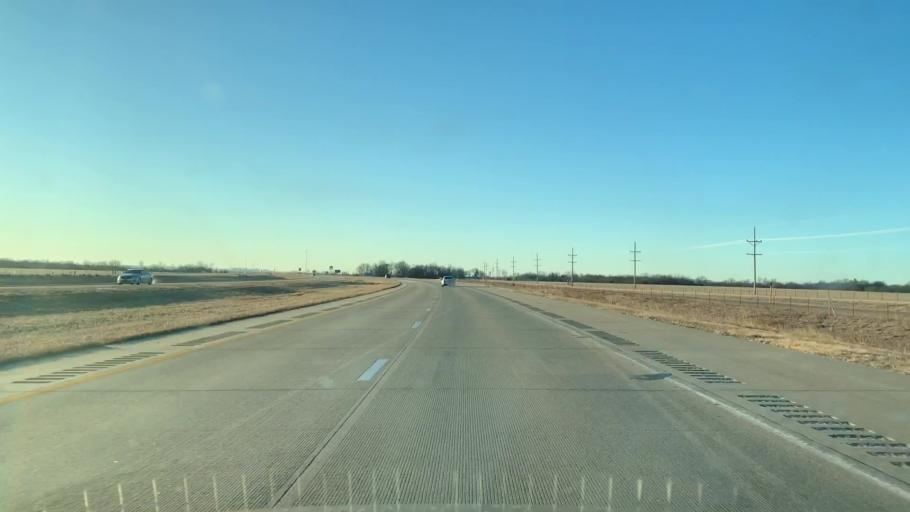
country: US
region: Kansas
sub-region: Linn County
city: Pleasanton
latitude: 38.1941
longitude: -94.7055
